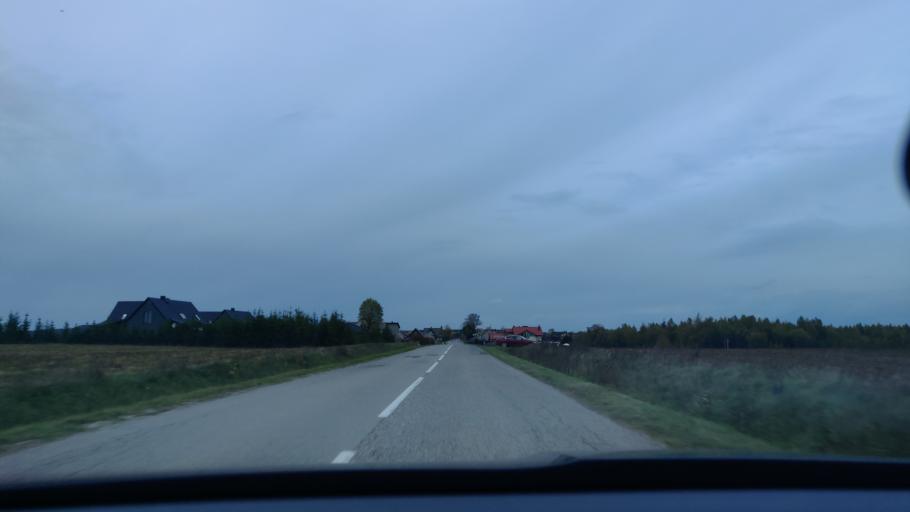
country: LT
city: Lentvaris
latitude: 54.5777
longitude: 25.0518
